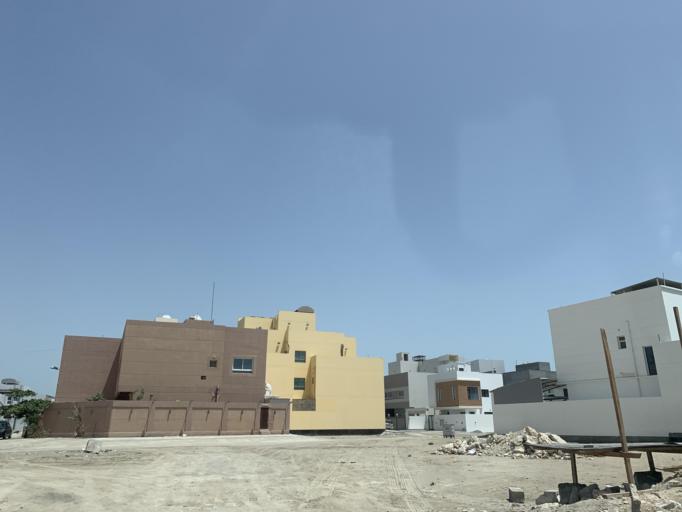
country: BH
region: Northern
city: Sitrah
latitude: 26.1493
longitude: 50.6004
